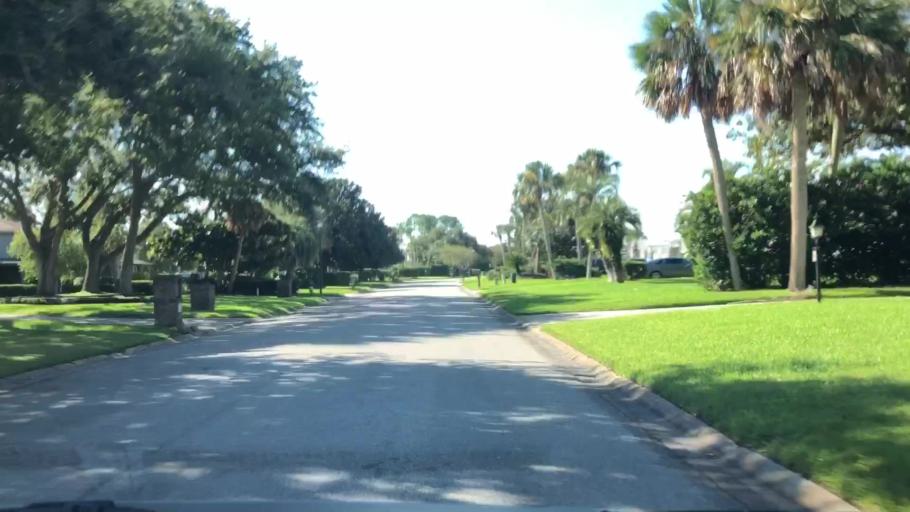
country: US
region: Florida
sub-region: Saint Johns County
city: Ponte Vedra Beach
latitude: 30.2390
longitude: -81.3847
